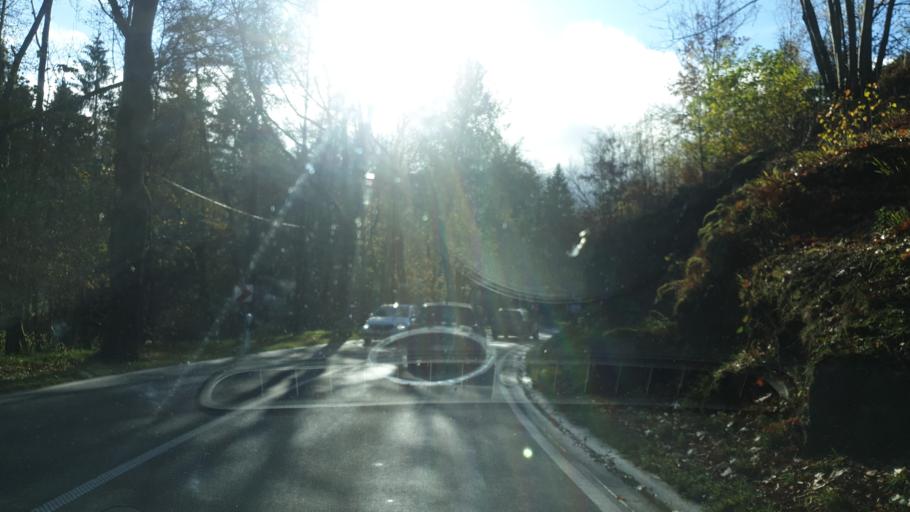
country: DE
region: Saxony
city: Sosa
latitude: 50.5169
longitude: 12.6342
